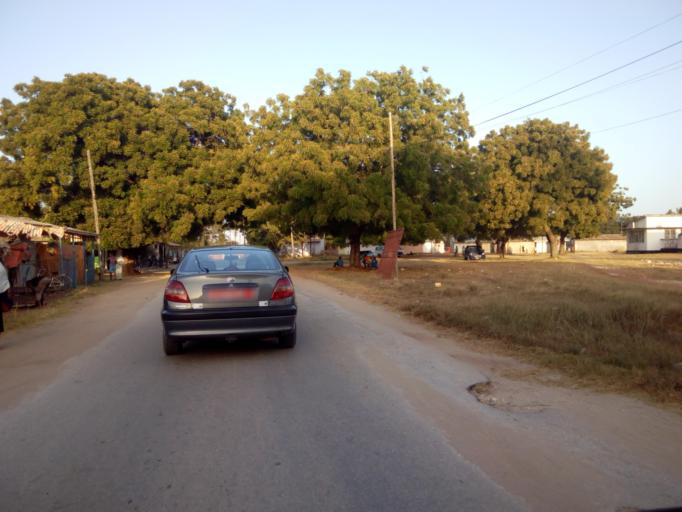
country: TZ
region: Zanzibar Urban/West
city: Zanzibar
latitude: -6.2068
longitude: 39.2088
